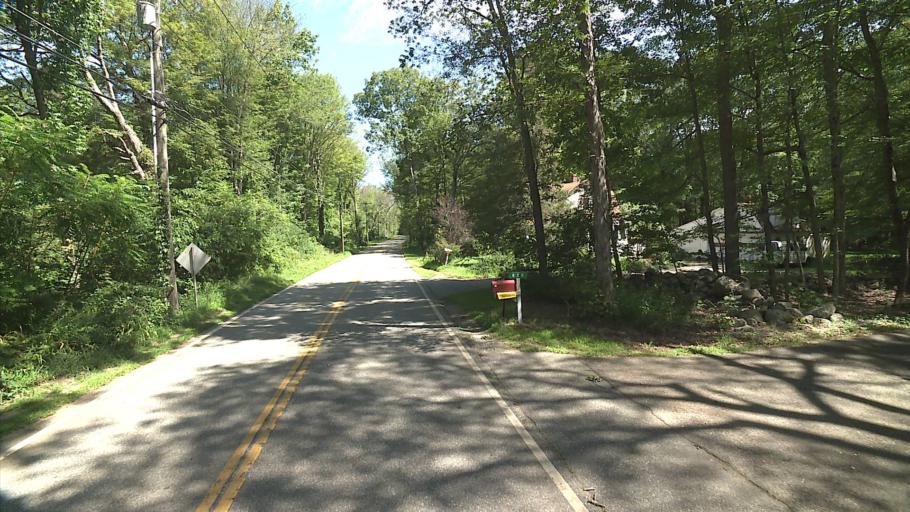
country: US
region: Connecticut
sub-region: Windham County
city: Windham
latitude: 41.7539
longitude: -72.0624
